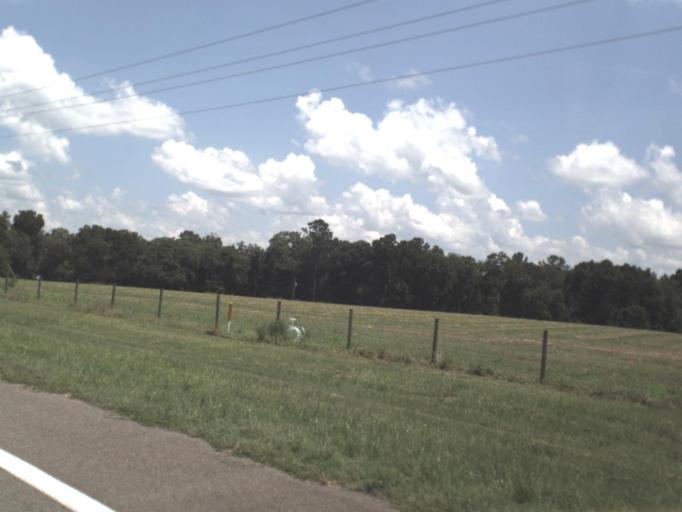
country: US
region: Florida
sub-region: Alachua County
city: Alachua
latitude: 29.8746
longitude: -82.4127
